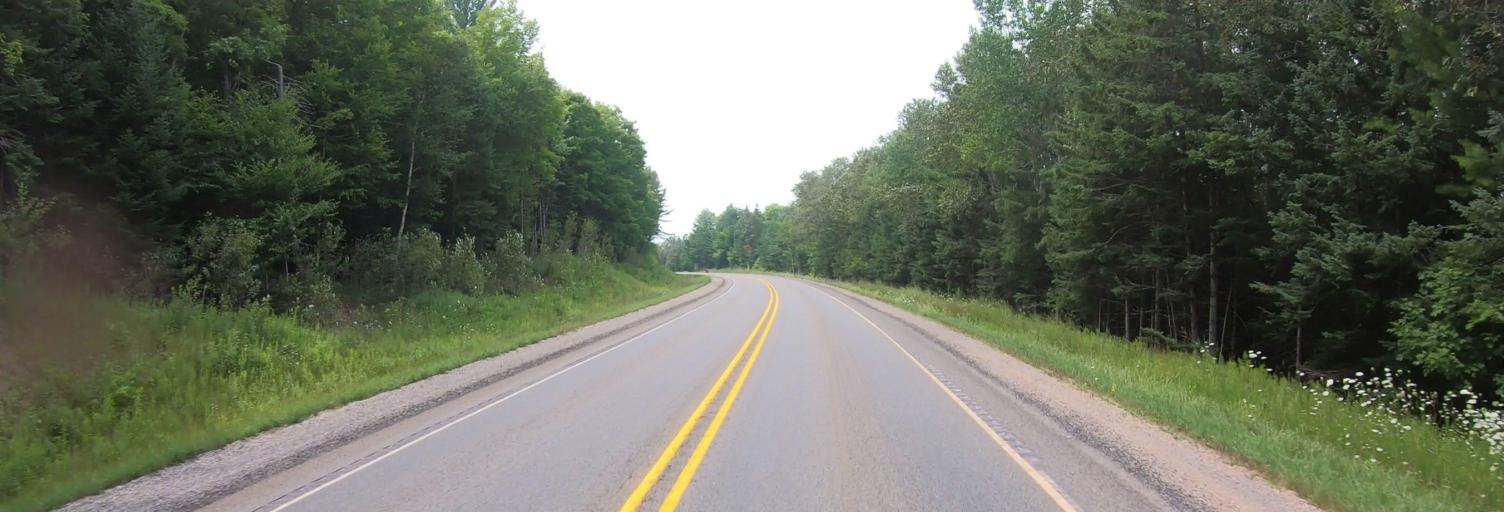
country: US
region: Michigan
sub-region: Alger County
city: Munising
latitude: 46.3338
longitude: -86.8318
